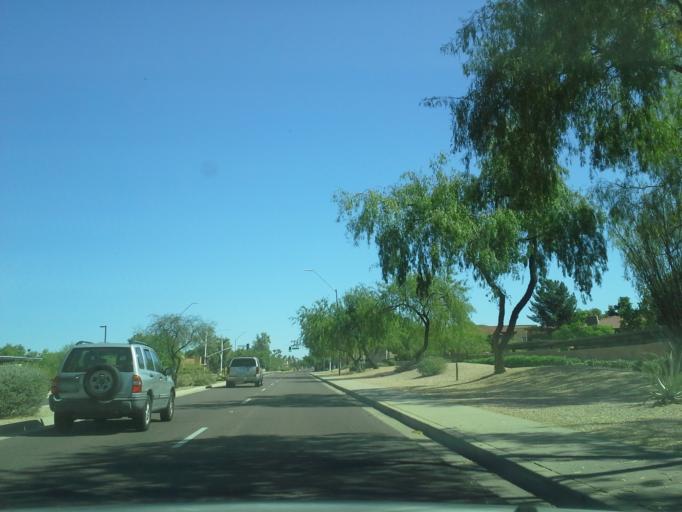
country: US
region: Arizona
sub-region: Maricopa County
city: Paradise Valley
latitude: 33.5769
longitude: -111.9303
